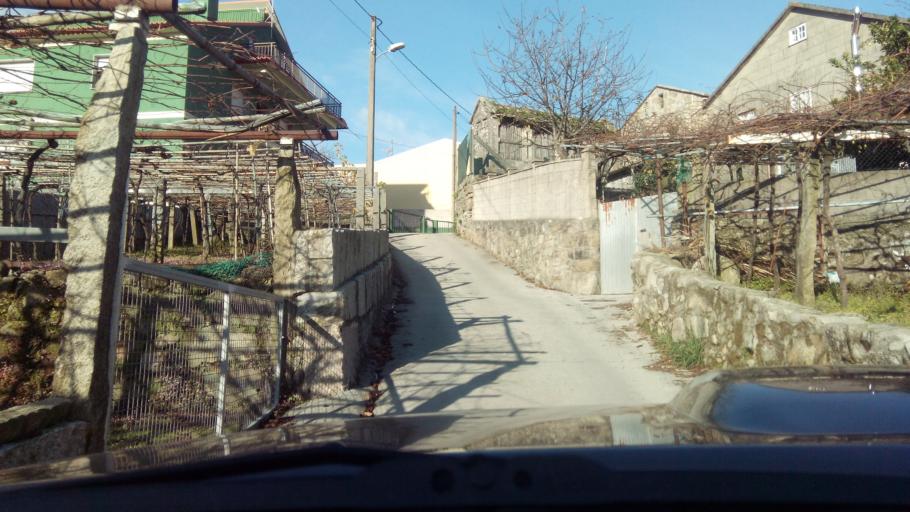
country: ES
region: Galicia
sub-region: Provincia de Pontevedra
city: Marin
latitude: 42.3622
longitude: -8.7032
